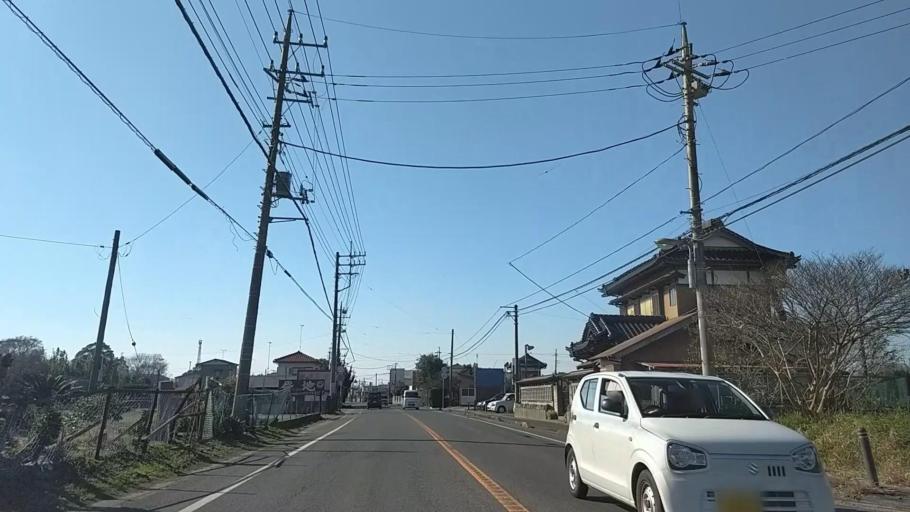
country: JP
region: Chiba
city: Yokaichiba
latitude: 35.7128
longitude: 140.5782
